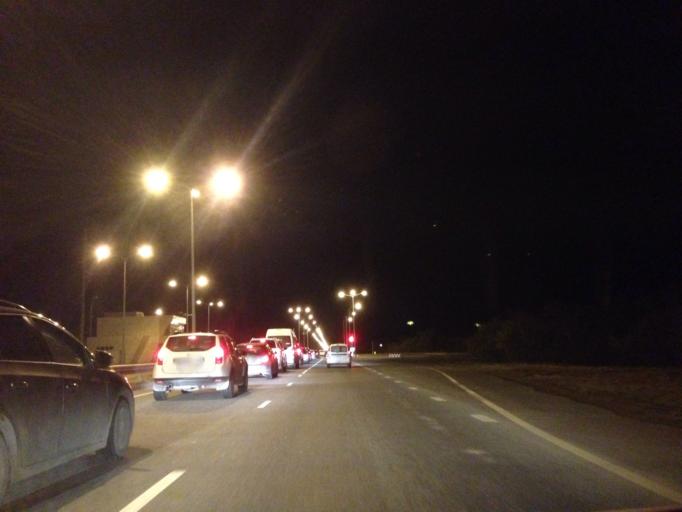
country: KZ
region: Astana Qalasy
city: Astana
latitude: 51.0132
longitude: 71.3809
